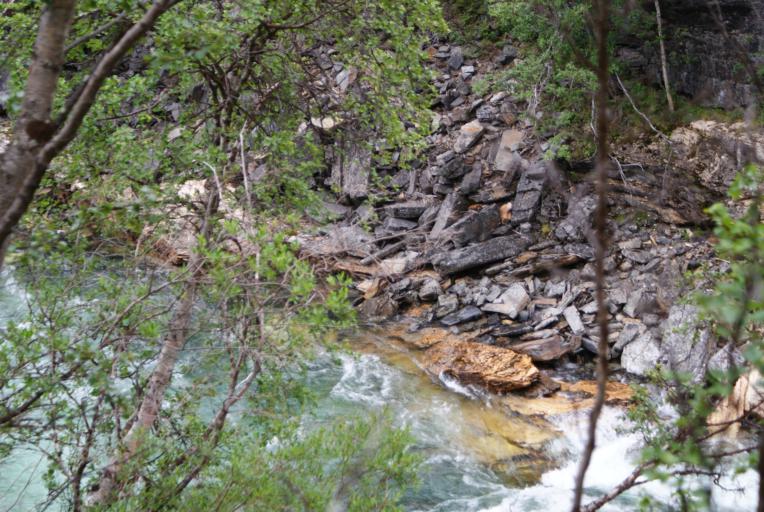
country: NO
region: Troms
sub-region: Bardu
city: Setermoen
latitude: 68.3599
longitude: 18.7810
